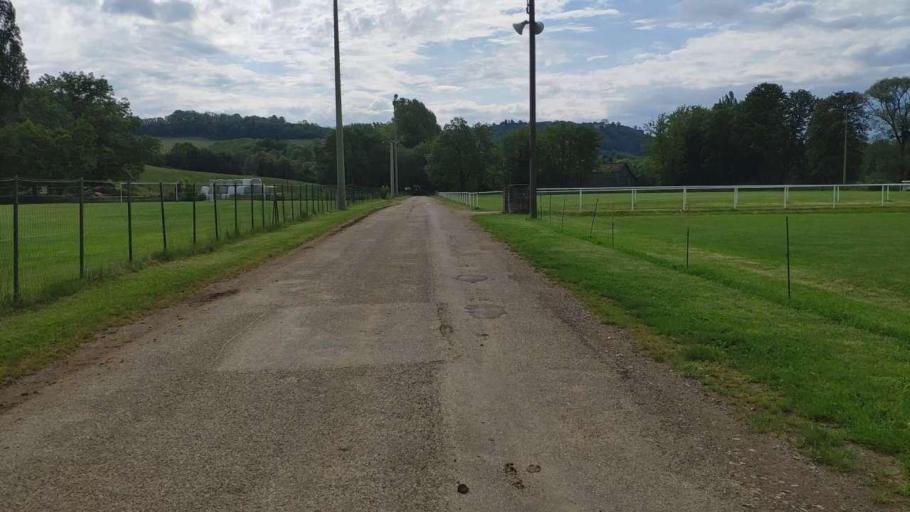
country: FR
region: Franche-Comte
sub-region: Departement du Jura
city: Perrigny
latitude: 46.7667
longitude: 5.6018
